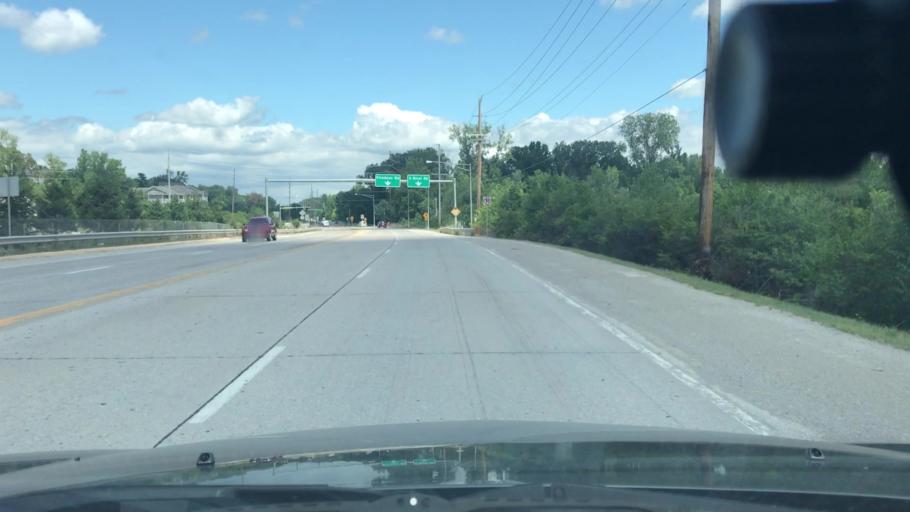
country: US
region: Missouri
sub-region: Saint Charles County
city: Saint Charles
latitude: 38.7530
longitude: -90.5037
